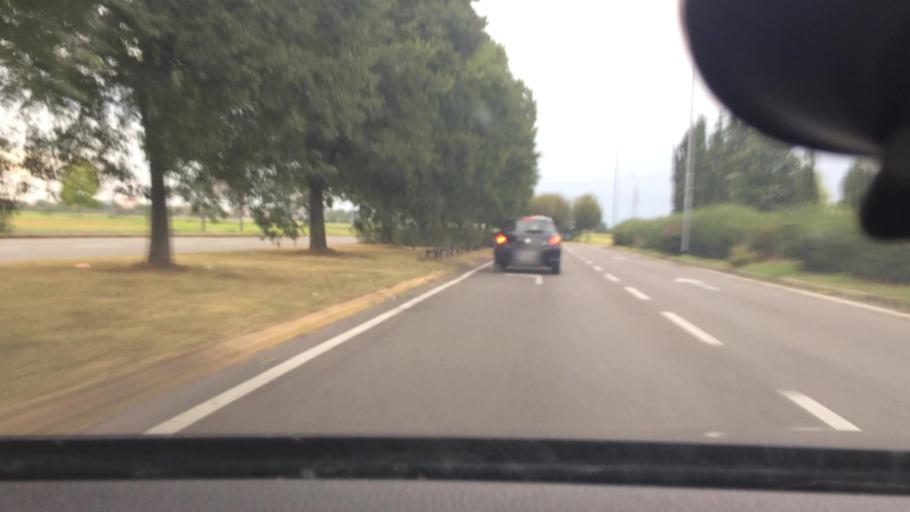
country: IT
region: Lombardy
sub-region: Citta metropolitana di Milano
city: Cusano Milanino
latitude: 45.5616
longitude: 9.1979
